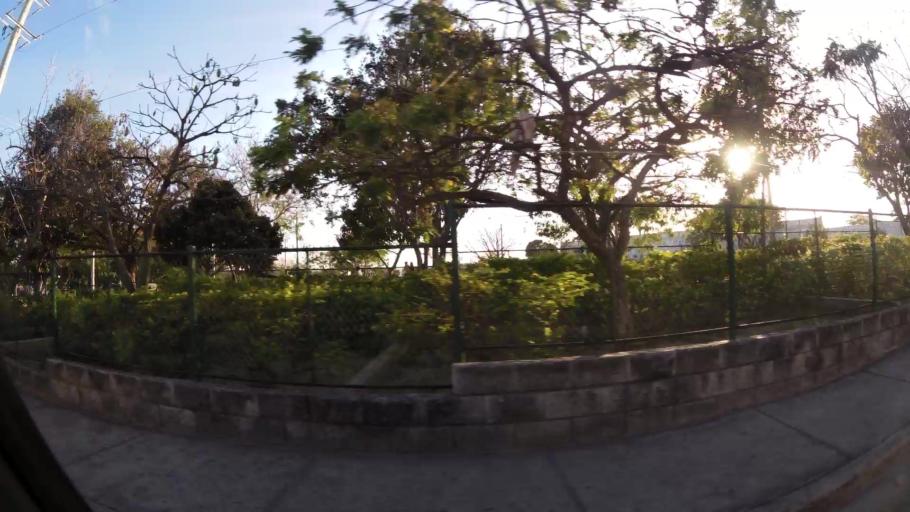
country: CO
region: Atlantico
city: Barranquilla
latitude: 10.9753
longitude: -74.7922
